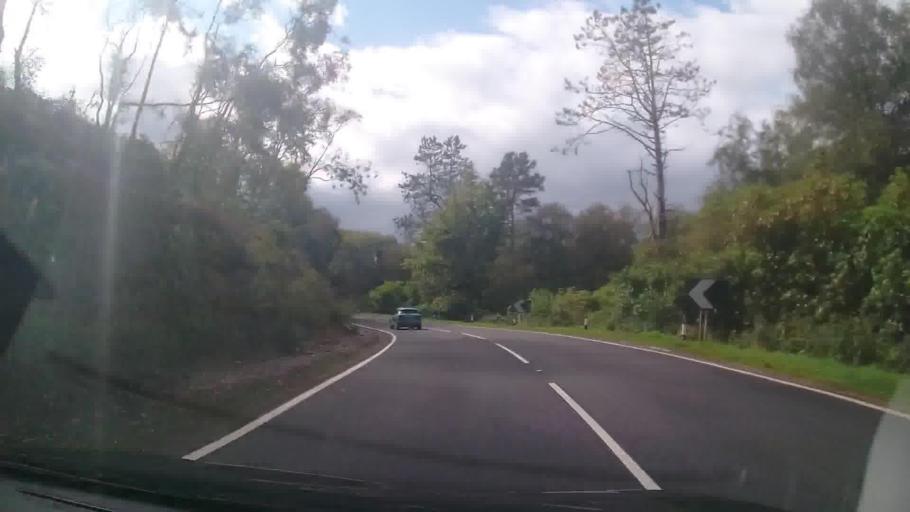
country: GB
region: Scotland
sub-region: Argyll and Bute
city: Oban
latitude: 56.5777
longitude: -5.3757
